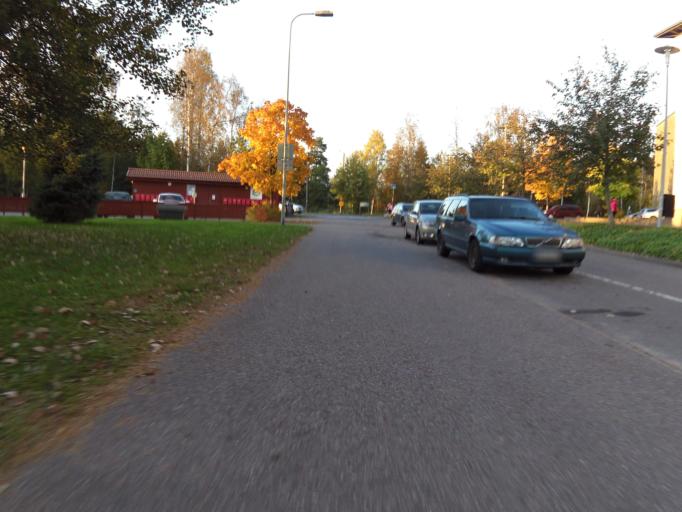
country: FI
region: Uusimaa
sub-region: Helsinki
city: Kilo
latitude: 60.2776
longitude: 24.7527
